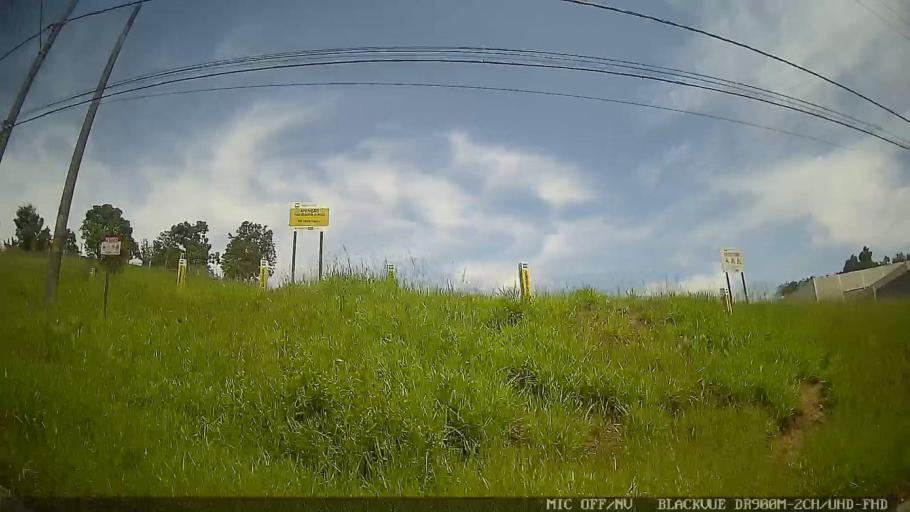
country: BR
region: Sao Paulo
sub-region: Santa Isabel
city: Santa Isabel
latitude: -23.3620
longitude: -46.1828
